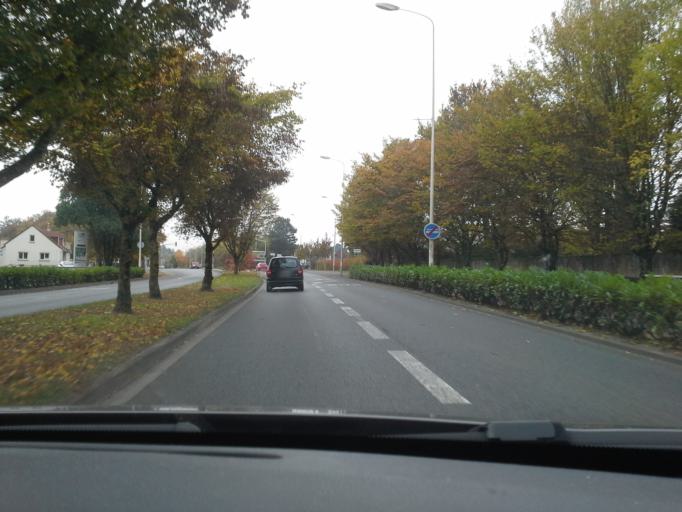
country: FR
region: Centre
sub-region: Departement d'Indre-et-Loire
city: Tours
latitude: 47.4139
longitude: 0.7030
